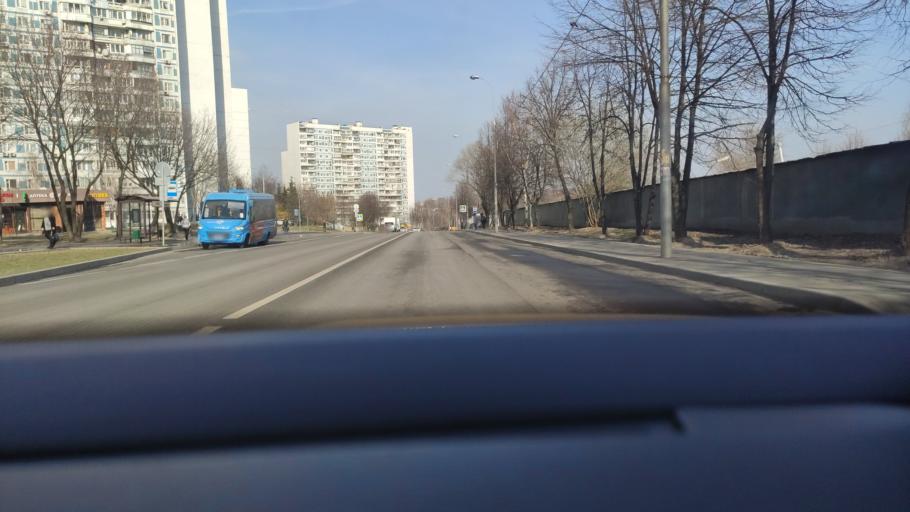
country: RU
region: Moscow
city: Zyablikovo
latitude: 55.6074
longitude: 37.7552
